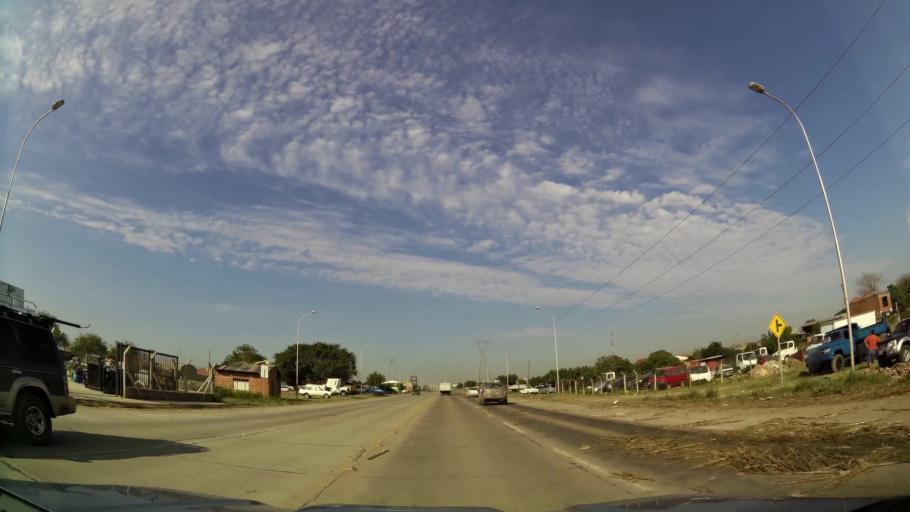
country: BO
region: Santa Cruz
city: Santa Cruz de la Sierra
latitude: -17.7250
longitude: -63.1343
